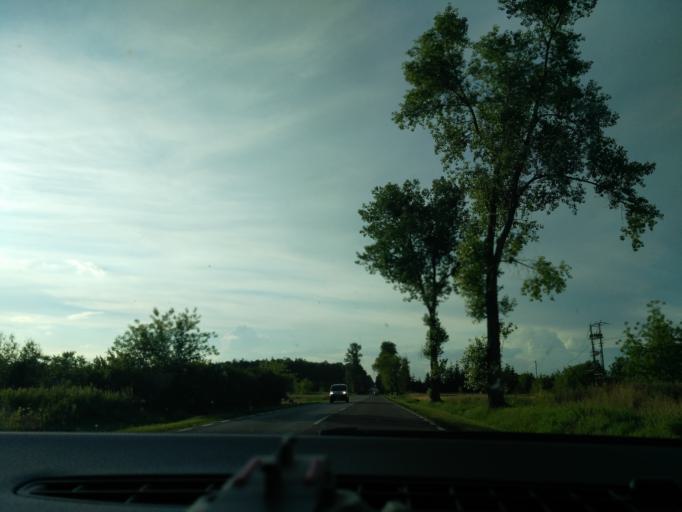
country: PL
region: Lublin Voivodeship
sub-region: Powiat krasnicki
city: Szastarka
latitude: 50.8668
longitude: 22.2745
